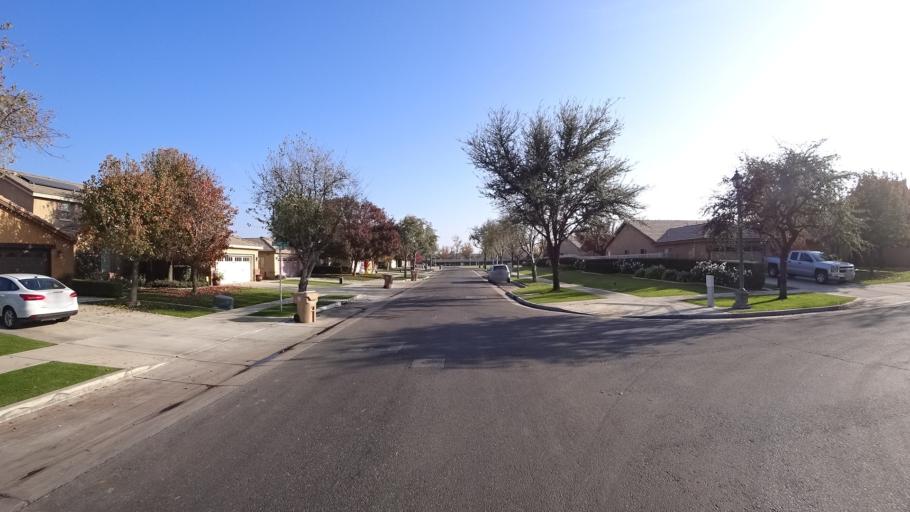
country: US
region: California
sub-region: Kern County
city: Rosedale
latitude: 35.3590
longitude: -119.1421
